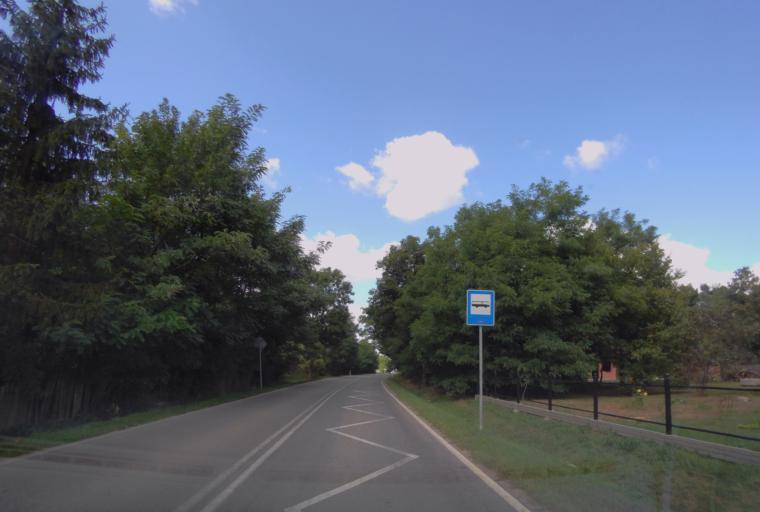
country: PL
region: Subcarpathian Voivodeship
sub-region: Powiat nizanski
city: Jezowe
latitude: 50.3833
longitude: 22.1062
